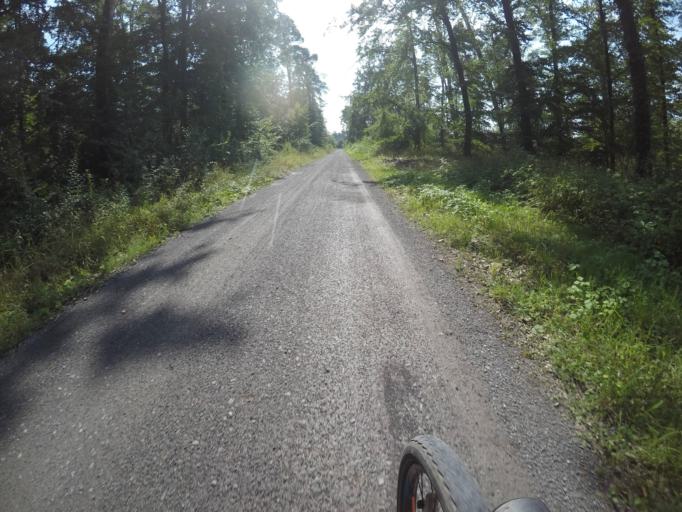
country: DE
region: Baden-Wuerttemberg
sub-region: Karlsruhe Region
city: Hockenheim
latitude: 49.3344
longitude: 8.5791
